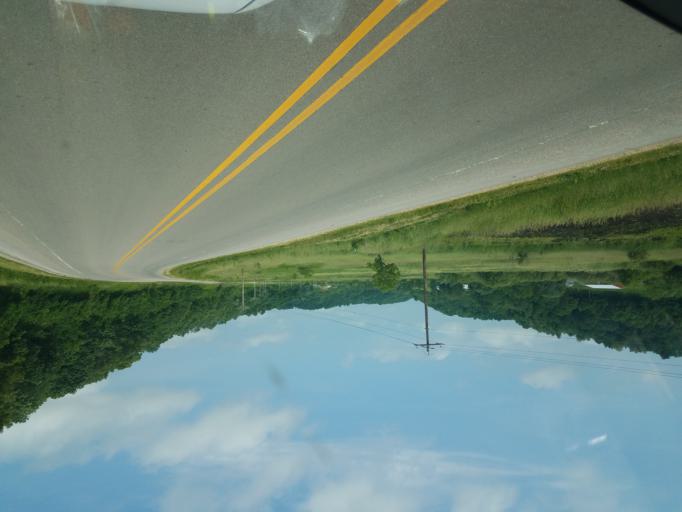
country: US
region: Wisconsin
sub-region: Monroe County
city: Cashton
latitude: 43.7345
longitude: -90.6950
